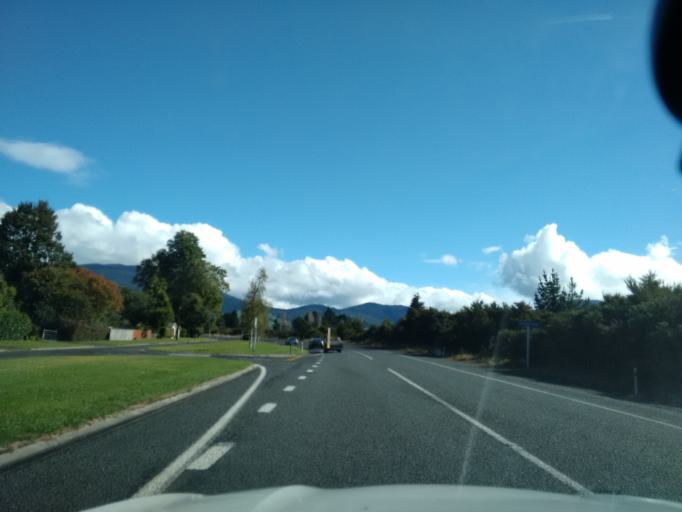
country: NZ
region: Waikato
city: Turangi
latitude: -38.9823
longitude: 175.8216
